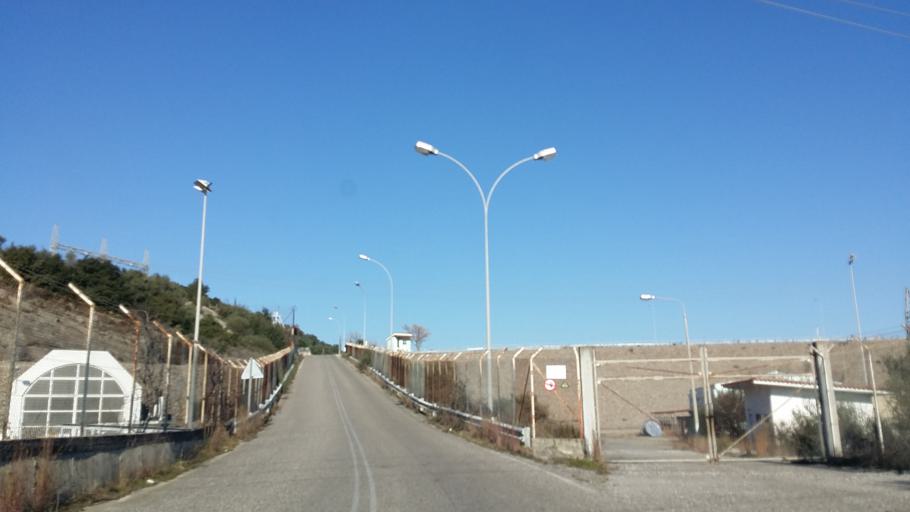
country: GR
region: West Greece
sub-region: Nomos Aitolias kai Akarnanias
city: Neapolis
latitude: 38.6749
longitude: 21.3252
